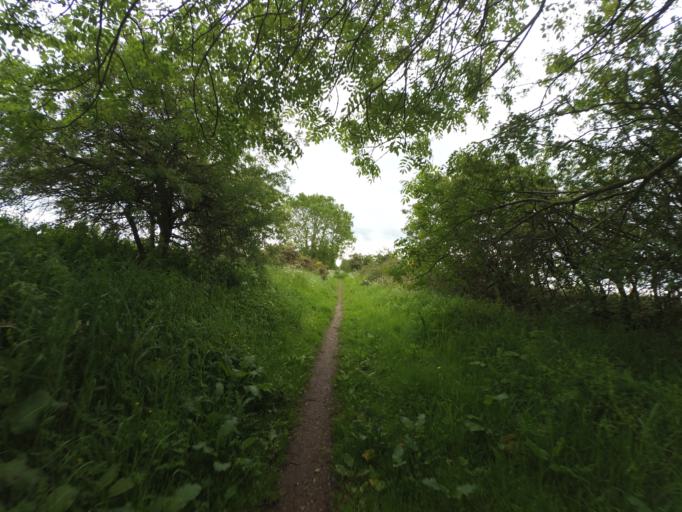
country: GB
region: Scotland
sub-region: East Lothian
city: Tranent
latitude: 55.9250
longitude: -2.9776
